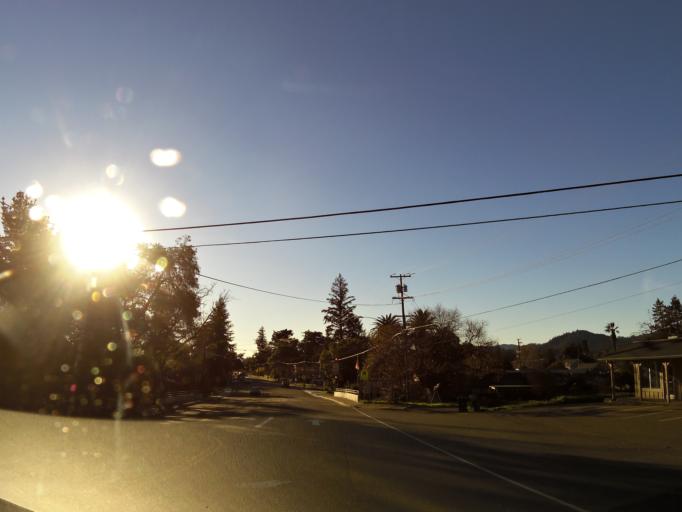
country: US
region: California
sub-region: Sonoma County
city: Cloverdale
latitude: 38.8139
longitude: -123.0233
